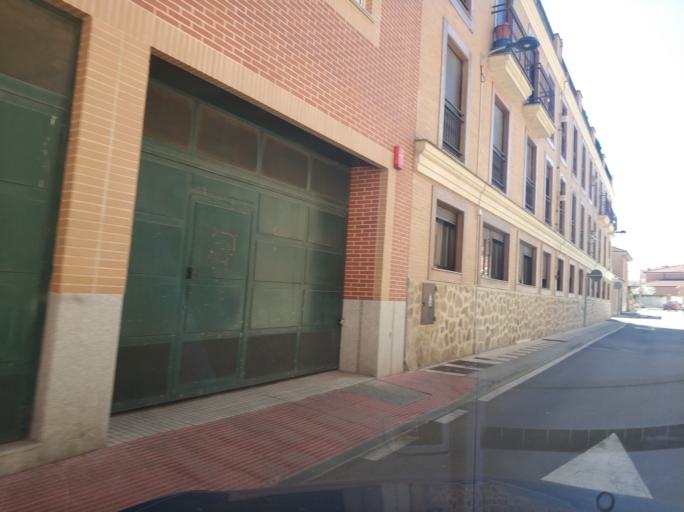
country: ES
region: Castille and Leon
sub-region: Provincia de Salamanca
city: Castellanos de Moriscos
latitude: 41.0185
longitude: -5.5885
